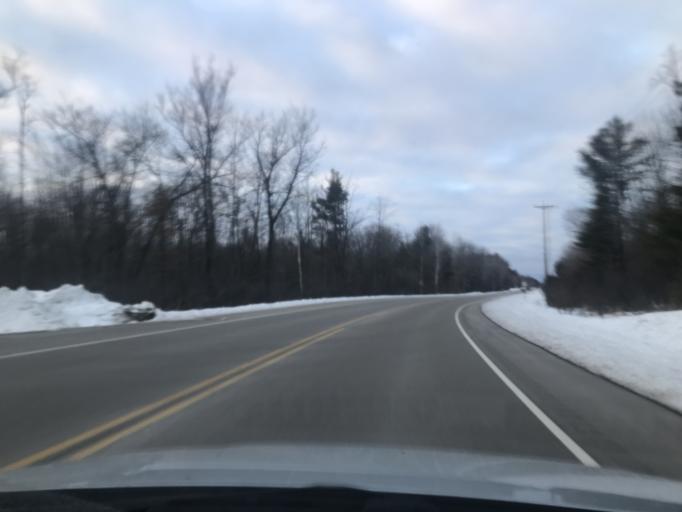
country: US
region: Wisconsin
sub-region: Marinette County
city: Marinette
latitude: 45.1165
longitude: -87.6806
